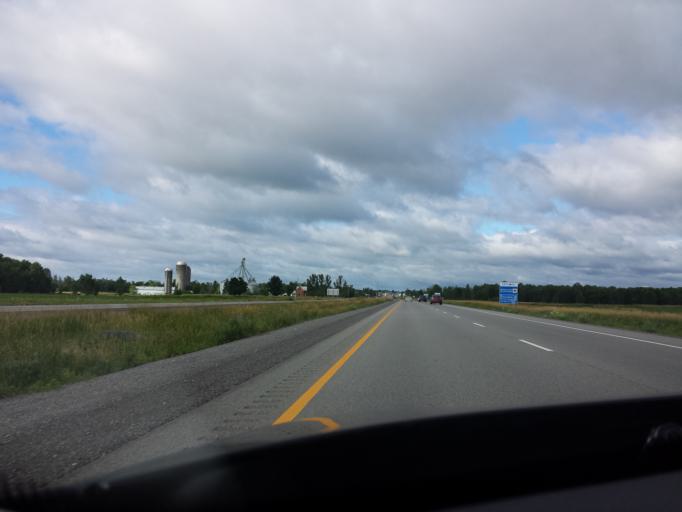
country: CA
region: Ontario
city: Carleton Place
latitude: 45.1438
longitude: -76.1022
